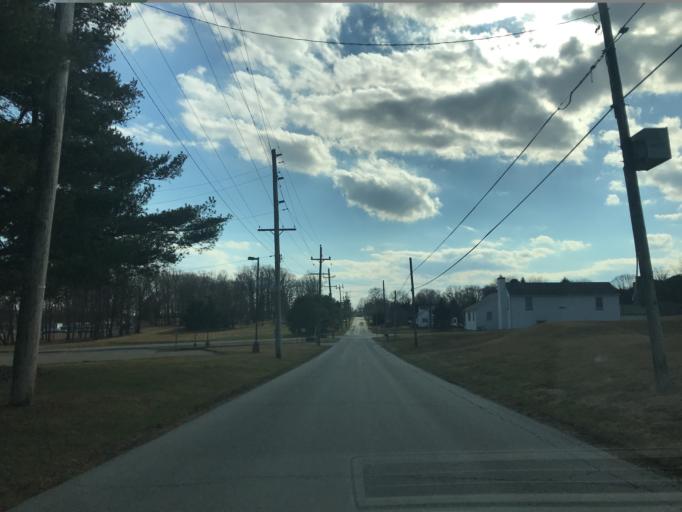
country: US
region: Pennsylvania
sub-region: Chester County
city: Oxford
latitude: 39.7473
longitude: -76.0199
